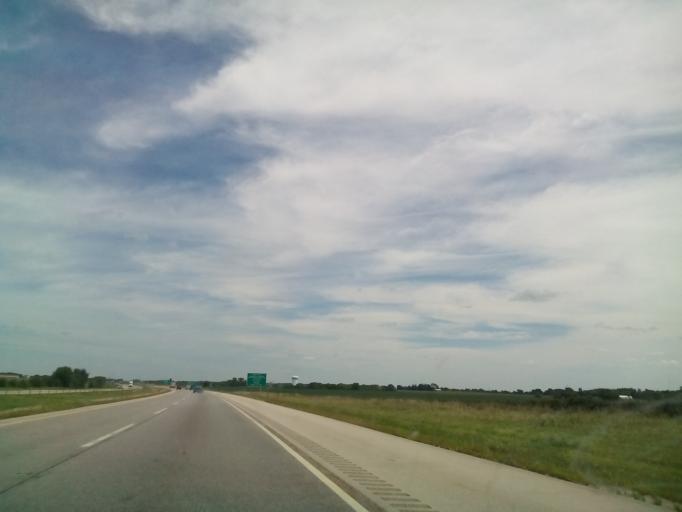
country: US
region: Illinois
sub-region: DeKalb County
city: DeKalb
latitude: 41.9002
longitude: -88.7951
